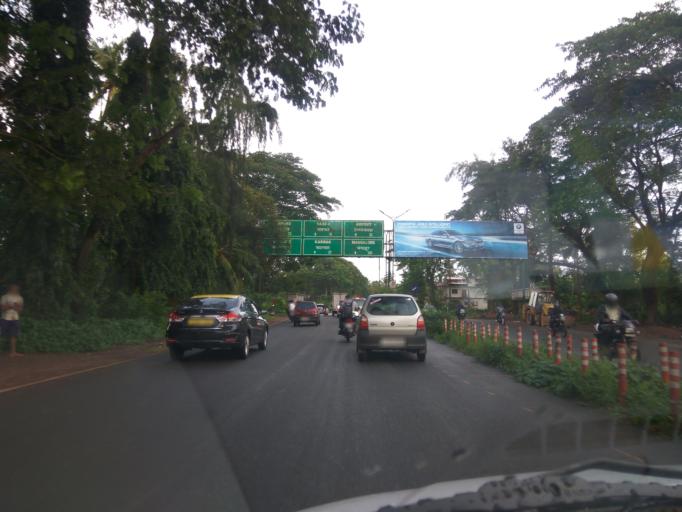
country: IN
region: Goa
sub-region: South Goa
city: Cortalim
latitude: 15.4223
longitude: 73.9010
